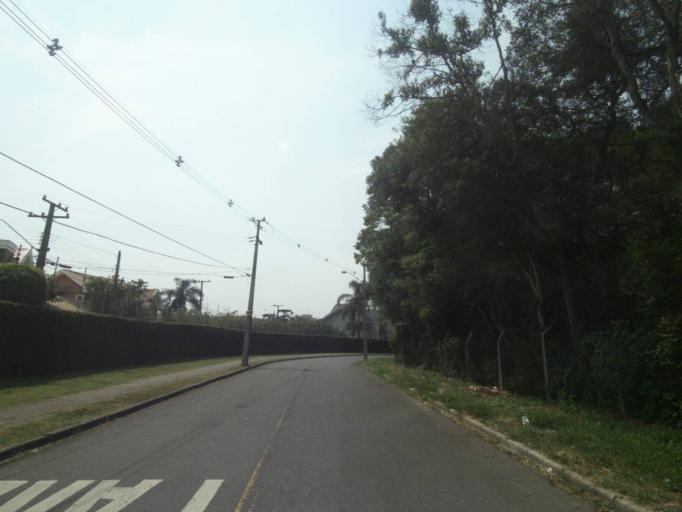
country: BR
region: Parana
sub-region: Sao Jose Dos Pinhais
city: Sao Jose dos Pinhais
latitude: -25.4875
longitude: -49.2102
